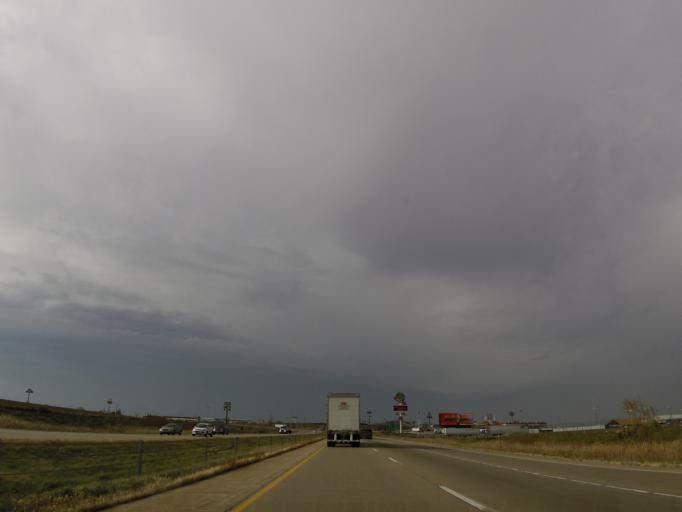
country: US
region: Iowa
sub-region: Scott County
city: Walcott
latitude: 41.6149
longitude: -90.7744
